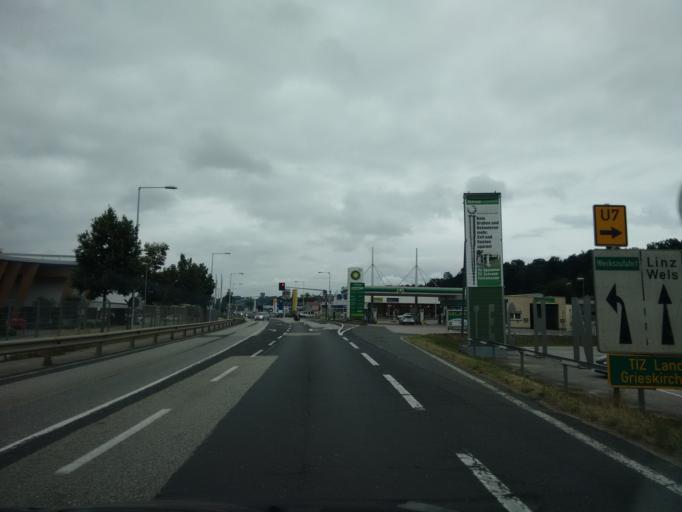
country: AT
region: Upper Austria
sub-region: Politischer Bezirk Grieskirchen
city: Grieskirchen
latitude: 48.2277
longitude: 13.8427
